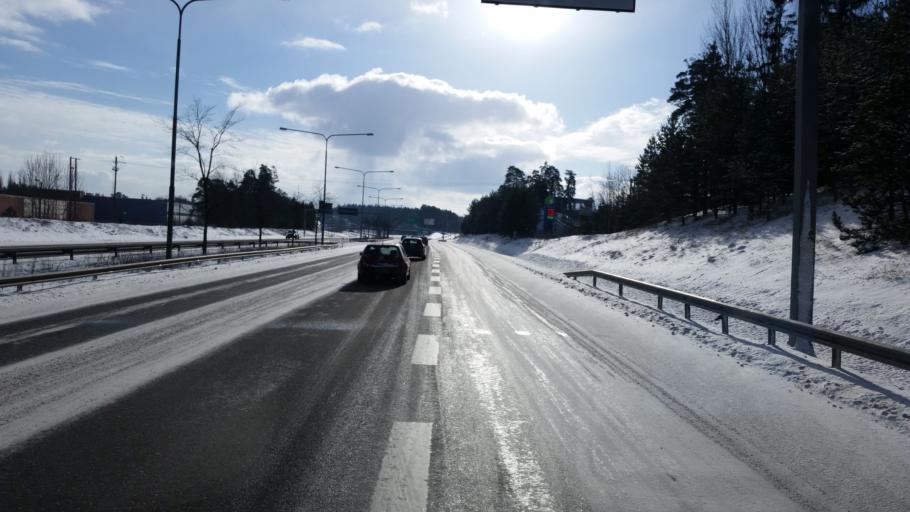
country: FI
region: Varsinais-Suomi
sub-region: Turku
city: Kaarina
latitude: 60.4334
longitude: 22.3218
